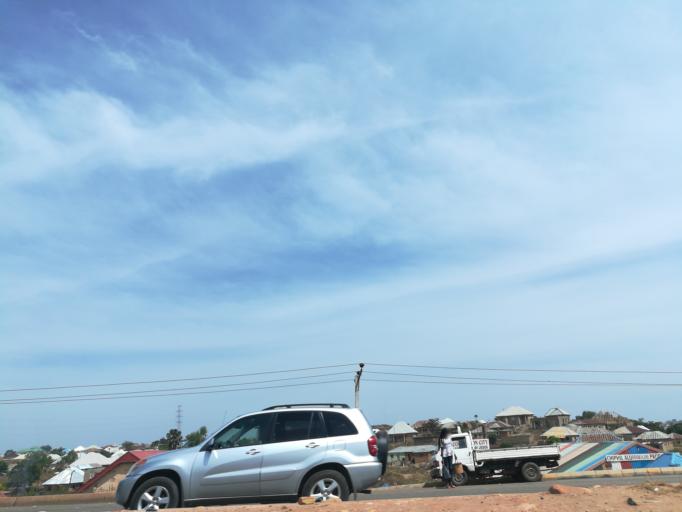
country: NG
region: Plateau
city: Bukuru
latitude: 9.8357
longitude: 8.8665
